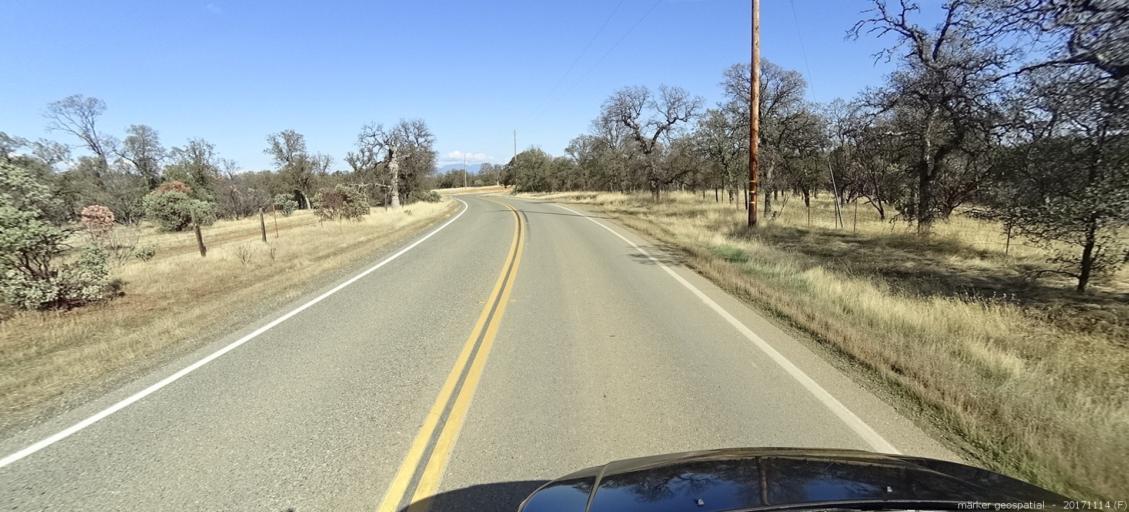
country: US
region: California
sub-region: Shasta County
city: Anderson
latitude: 40.4191
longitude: -122.3380
